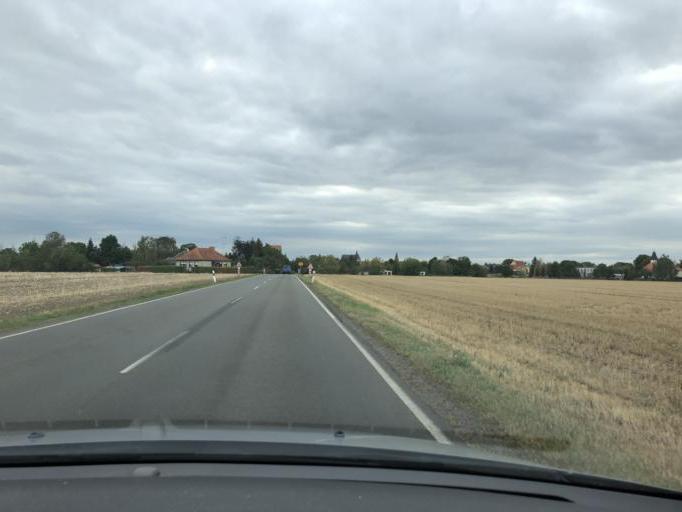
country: DE
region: Saxony-Anhalt
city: Zorbig
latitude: 51.6328
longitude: 12.1285
